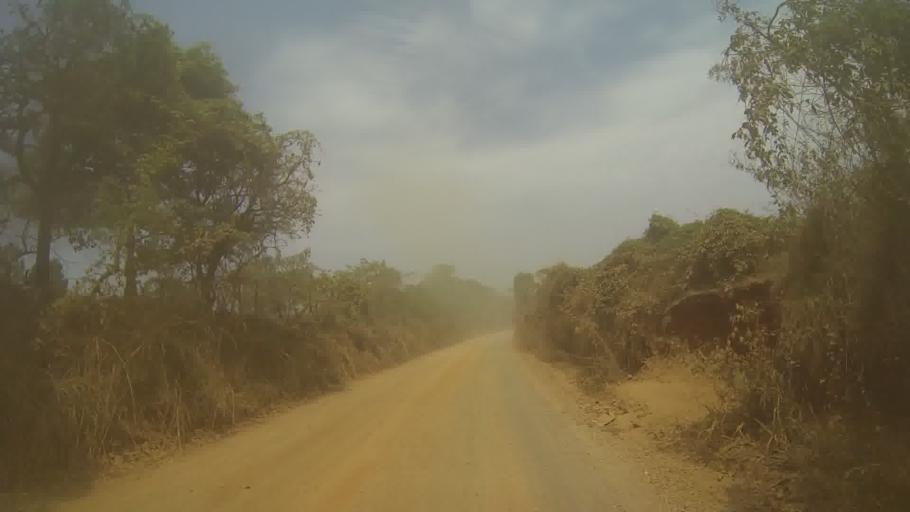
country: BR
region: Minas Gerais
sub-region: Bambui
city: Bambui
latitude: -20.0134
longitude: -45.9339
